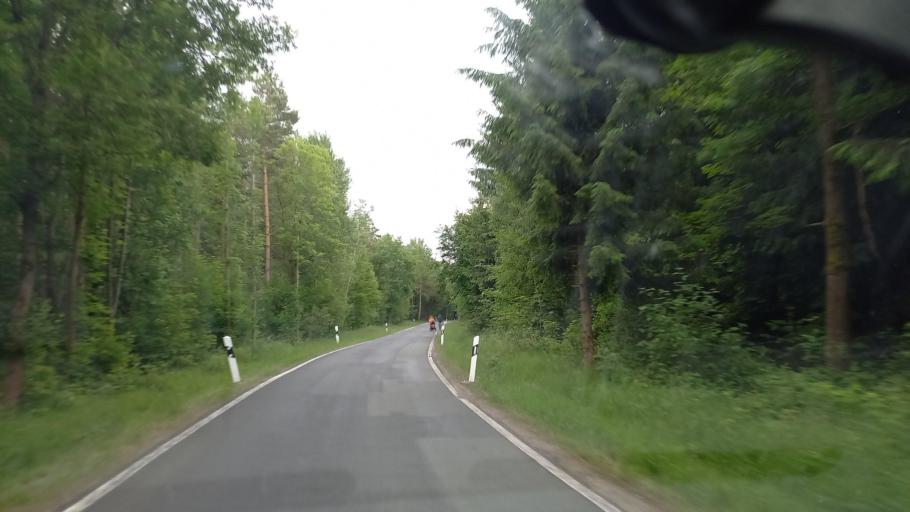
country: DE
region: Saxony
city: Waldkirchen
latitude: 50.6212
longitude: 12.4069
